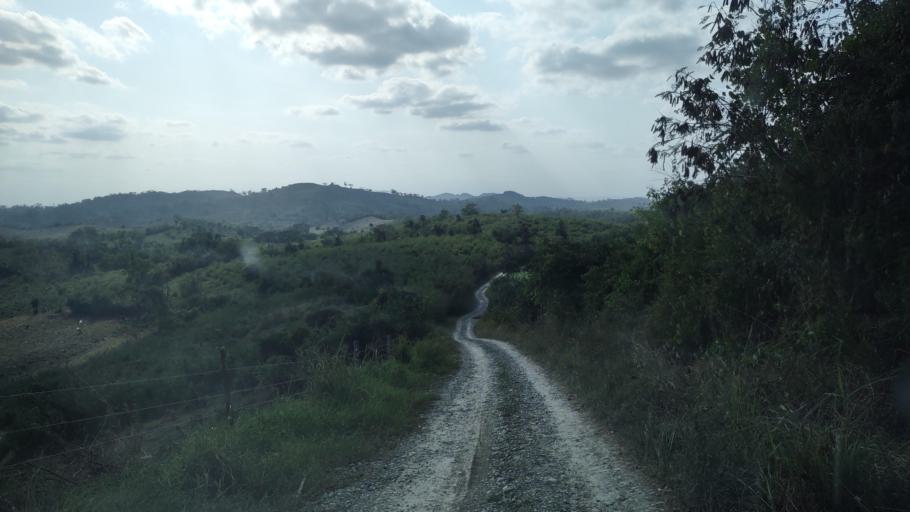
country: MX
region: Veracruz
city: Papantla de Olarte
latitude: 20.4574
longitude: -97.3964
